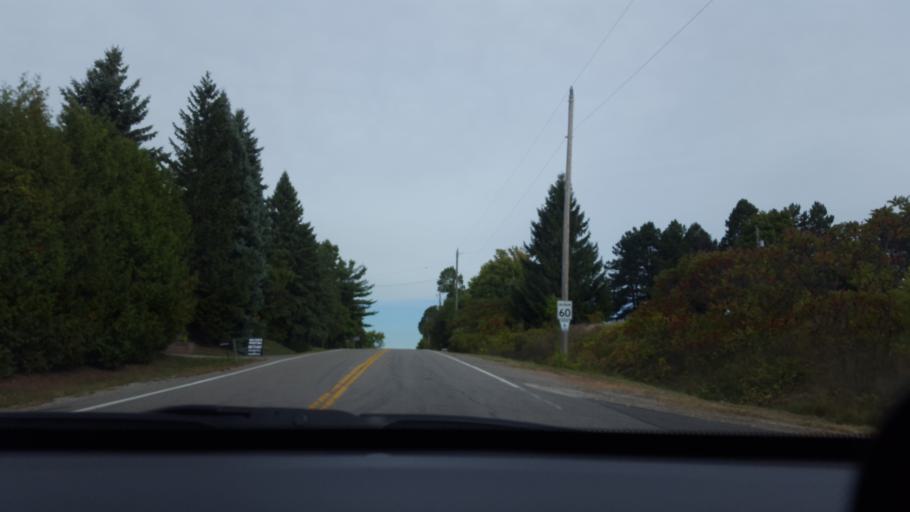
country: CA
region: Ontario
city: Newmarket
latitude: 43.9832
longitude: -79.5431
